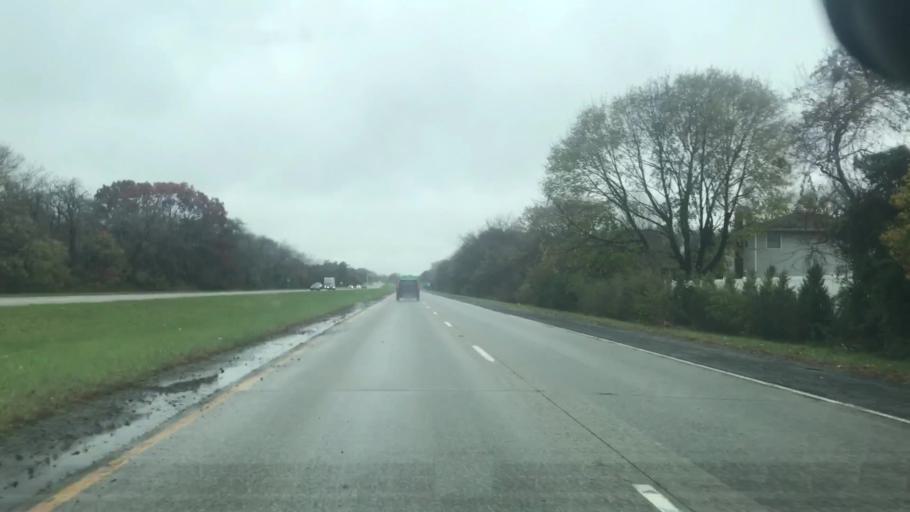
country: US
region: New York
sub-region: Suffolk County
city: West Islip
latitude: 40.7105
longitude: -73.3138
